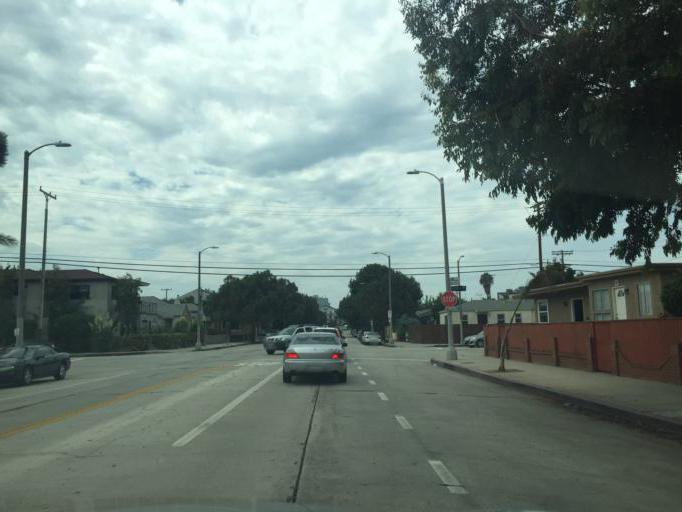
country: US
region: California
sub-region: Los Angeles County
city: Marina del Rey
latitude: 33.9875
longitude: -118.4681
